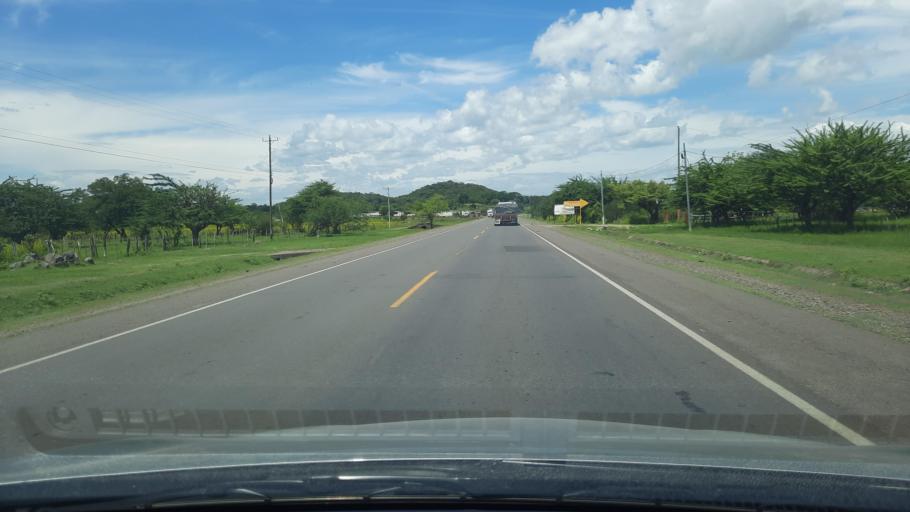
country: NI
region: Chinandega
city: Somotillo
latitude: 13.0551
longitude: -86.9180
